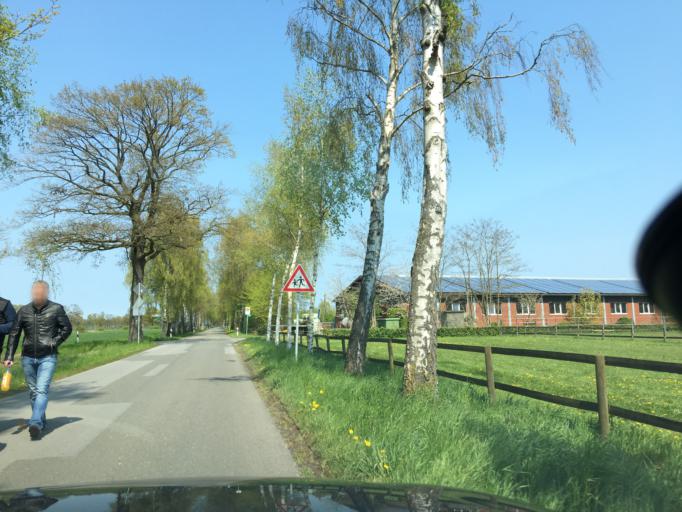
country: DE
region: North Rhine-Westphalia
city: Ludinghausen
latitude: 51.7994
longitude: 7.4338
